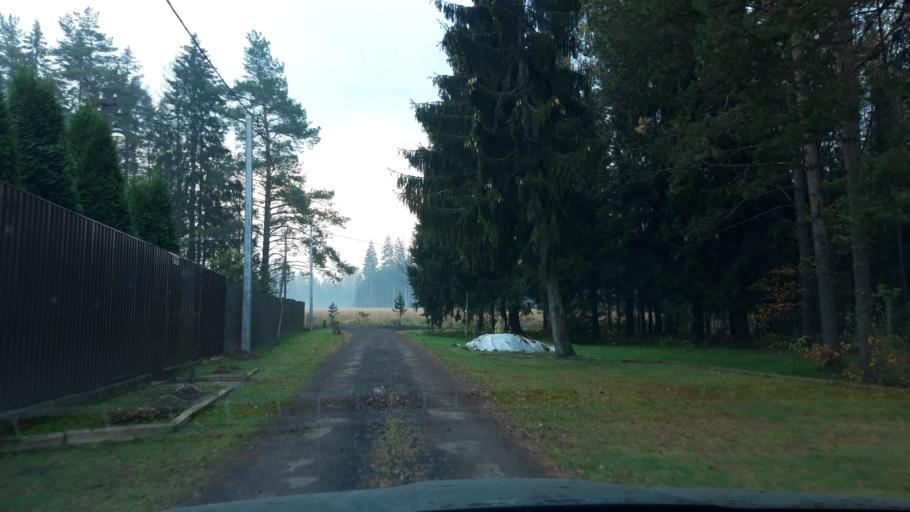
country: RU
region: Moskovskaya
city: Lozhki
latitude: 56.0493
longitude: 37.0974
